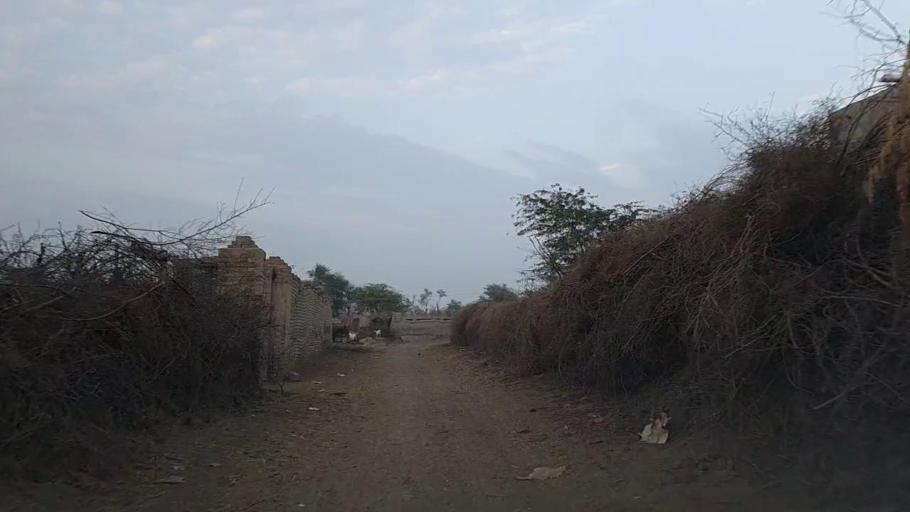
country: PK
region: Sindh
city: Jam Sahib
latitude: 26.2992
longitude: 68.5931
